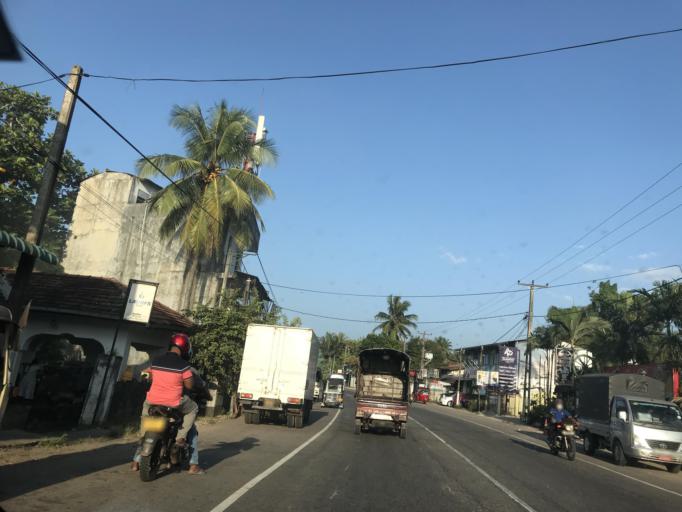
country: LK
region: Western
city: Ja Ela
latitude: 7.0872
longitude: 79.8977
